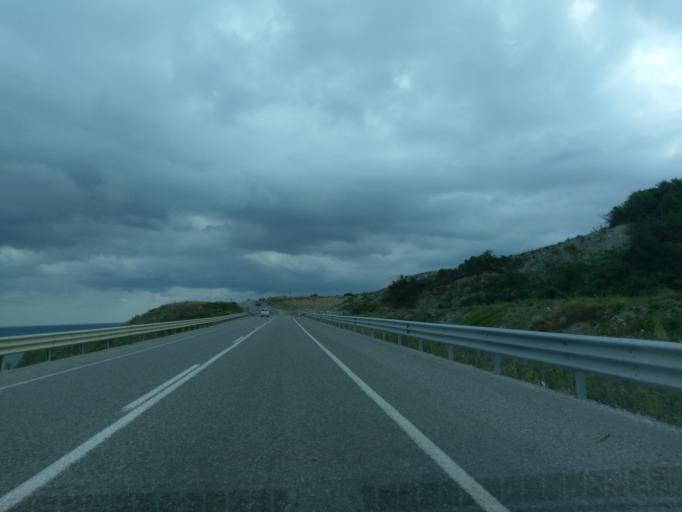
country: TR
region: Sinop
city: Helaldi
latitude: 41.9506
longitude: 34.3745
